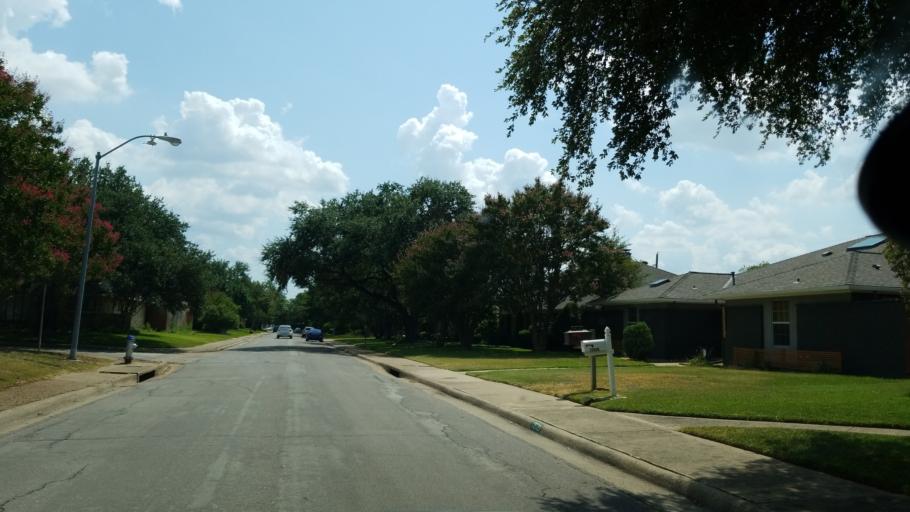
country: US
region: Texas
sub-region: Dallas County
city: Richardson
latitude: 32.9193
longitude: -96.7218
